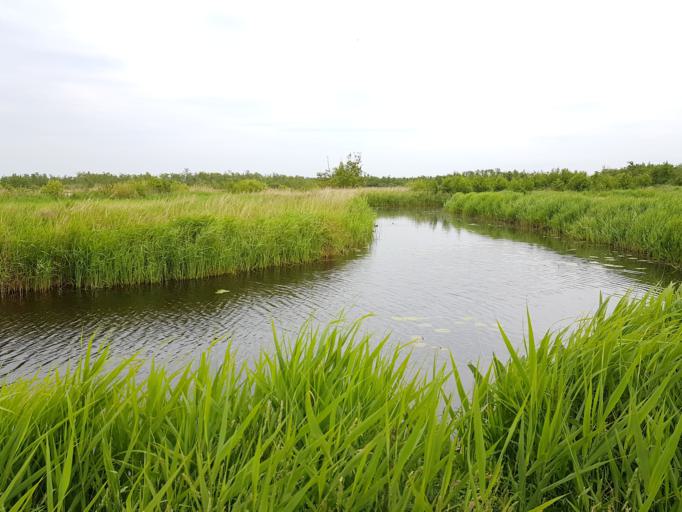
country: NL
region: Friesland
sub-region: Gemeente Boarnsterhim
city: Warten
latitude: 53.1410
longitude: 5.9270
